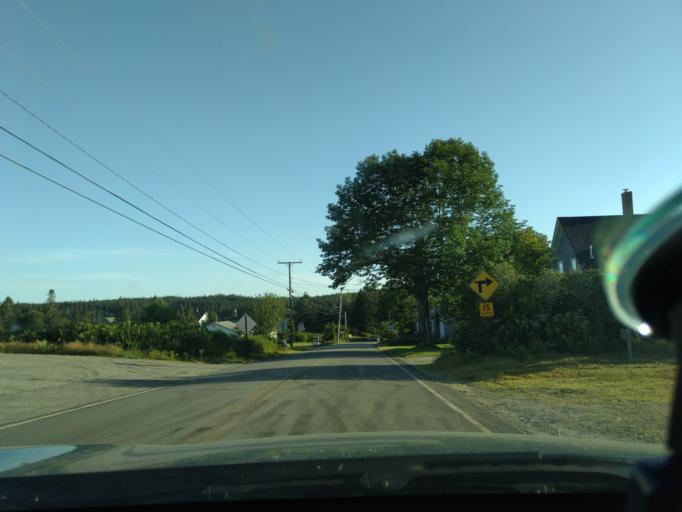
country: US
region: Maine
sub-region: Washington County
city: Machiasport
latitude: 44.6584
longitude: -67.2032
